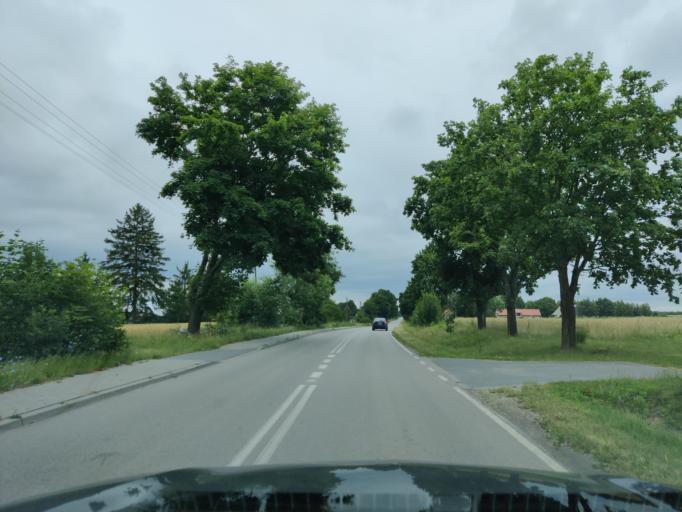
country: PL
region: Masovian Voivodeship
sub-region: Powiat pultuski
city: Pultusk
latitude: 52.7702
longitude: 21.0556
